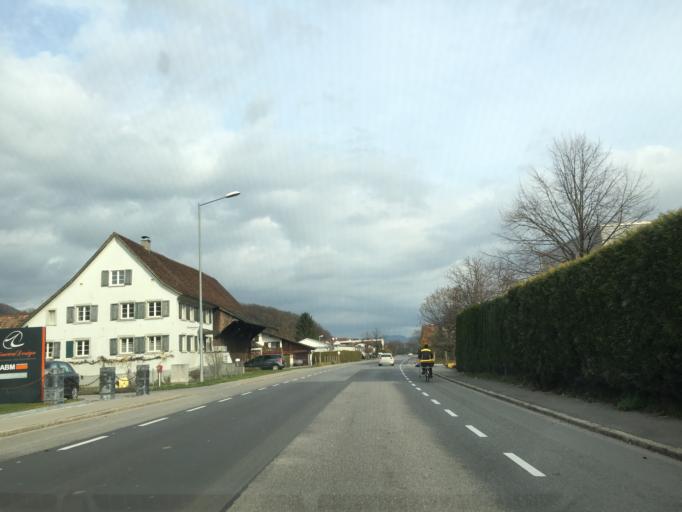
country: AT
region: Vorarlberg
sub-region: Politischer Bezirk Feldkirch
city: Gotzis
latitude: 47.3167
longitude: 9.6207
